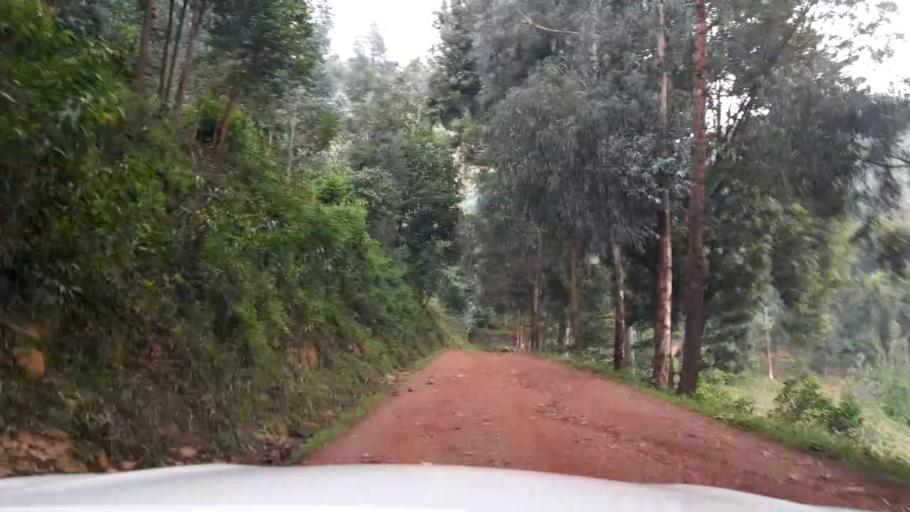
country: UG
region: Western Region
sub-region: Kisoro District
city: Kisoro
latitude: -1.3965
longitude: 29.8021
